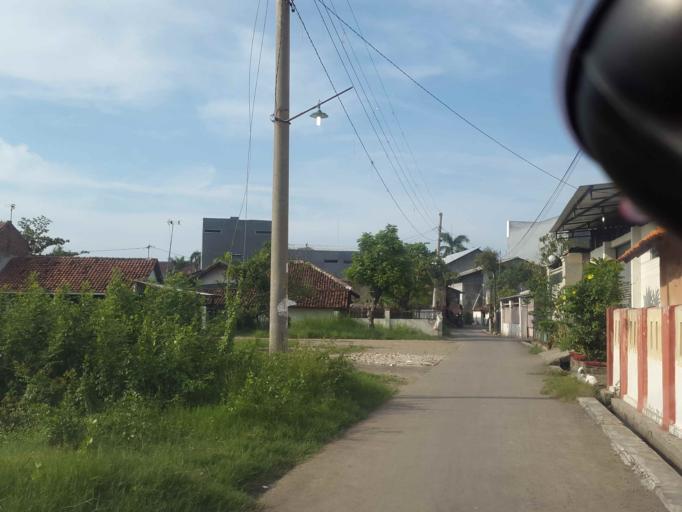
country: ID
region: Central Java
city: Tegal
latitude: -6.8565
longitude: 109.1413
